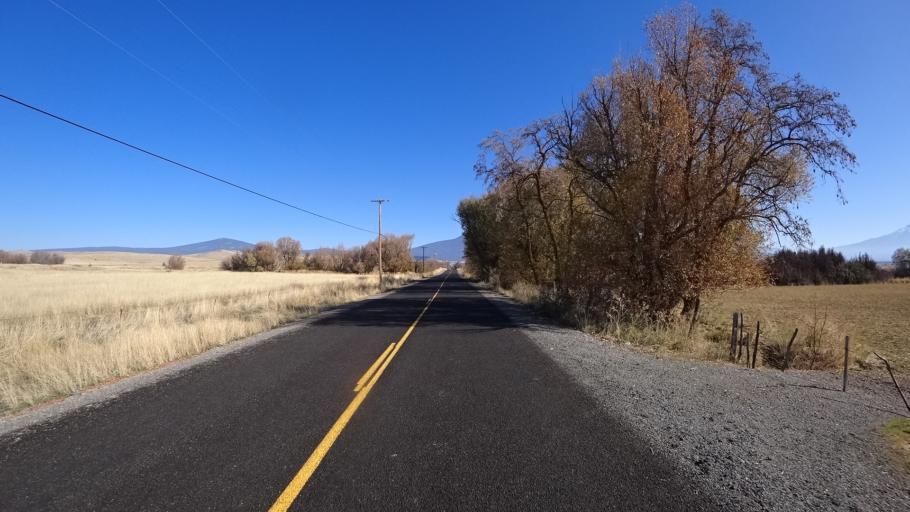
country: US
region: California
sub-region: Siskiyou County
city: Montague
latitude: 41.7263
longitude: -122.4193
